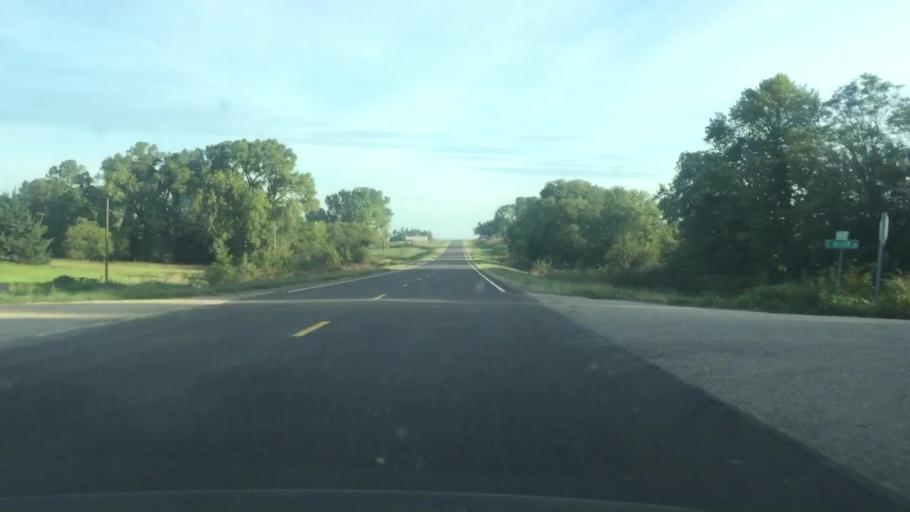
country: US
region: Nebraska
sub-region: Gage County
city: Wymore
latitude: 40.0158
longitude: -96.6522
